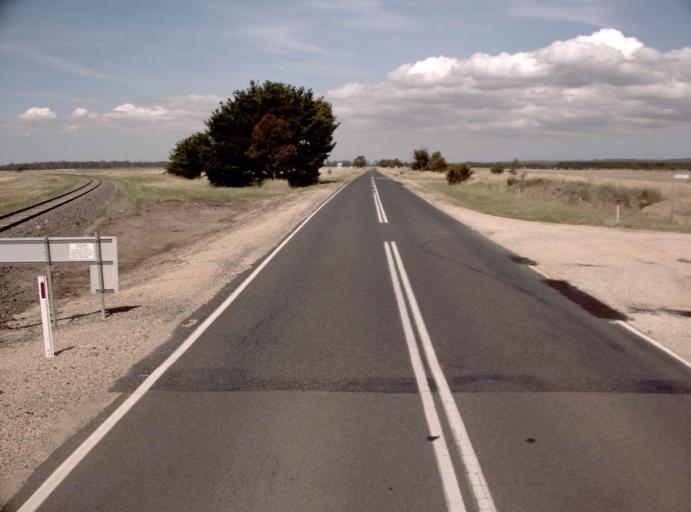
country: AU
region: Victoria
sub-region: Wellington
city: Heyfield
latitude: -38.1549
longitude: 146.8321
